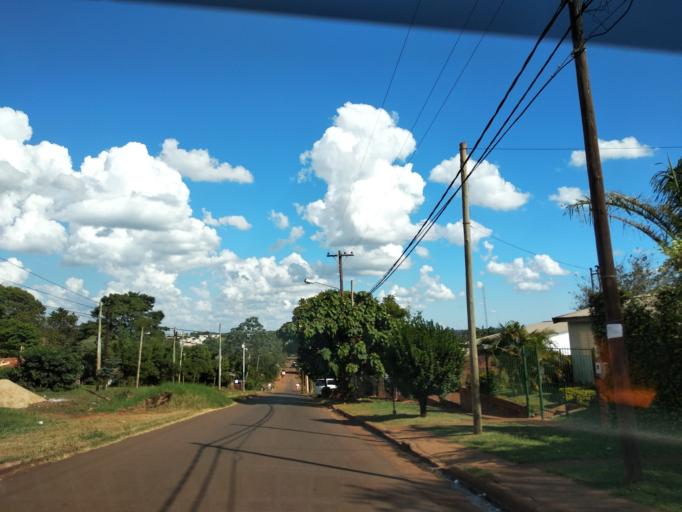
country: AR
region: Misiones
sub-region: Departamento de Capital
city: Posadas
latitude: -27.3852
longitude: -55.9457
